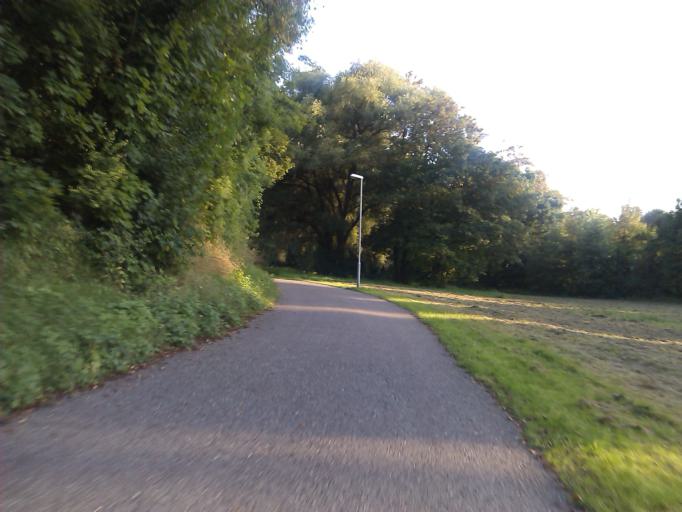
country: DE
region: Baden-Wuerttemberg
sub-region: Karlsruhe Region
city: Muhlhausen
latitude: 49.2541
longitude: 8.7209
